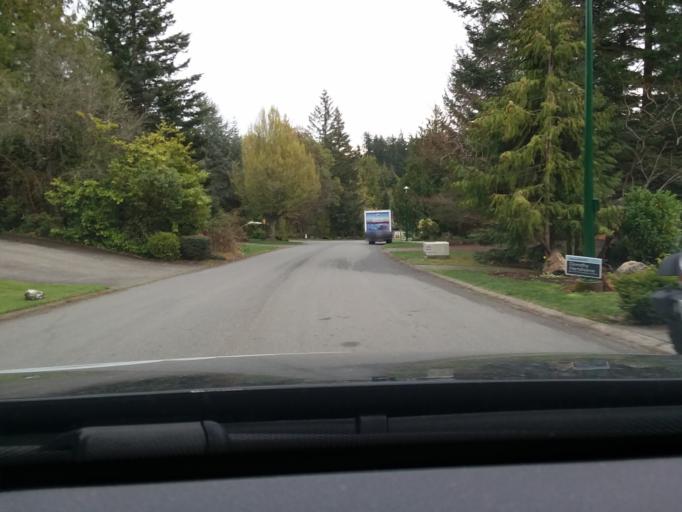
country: CA
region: British Columbia
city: North Saanich
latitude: 48.6151
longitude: -123.4249
